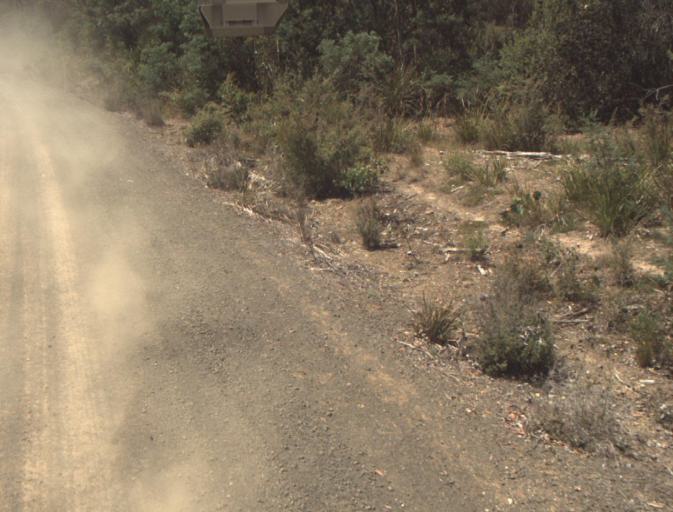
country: AU
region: Tasmania
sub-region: Launceston
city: Mayfield
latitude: -41.2788
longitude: 147.0969
